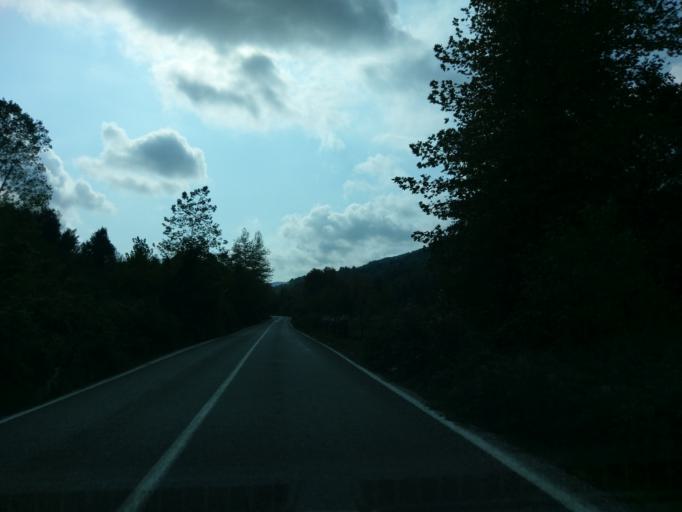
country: TR
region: Sinop
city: Helaldi
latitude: 41.9031
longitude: 34.4512
